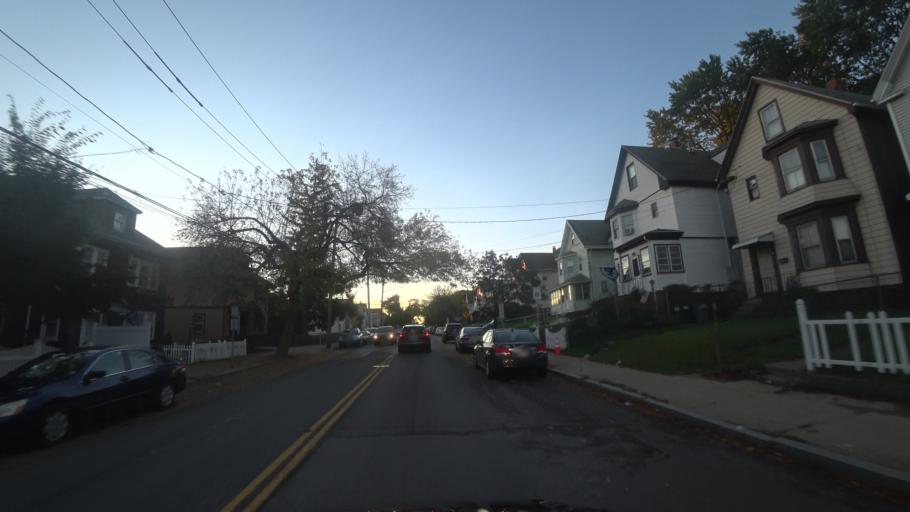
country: US
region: Massachusetts
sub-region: Suffolk County
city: Chelsea
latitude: 42.4035
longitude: -71.0285
